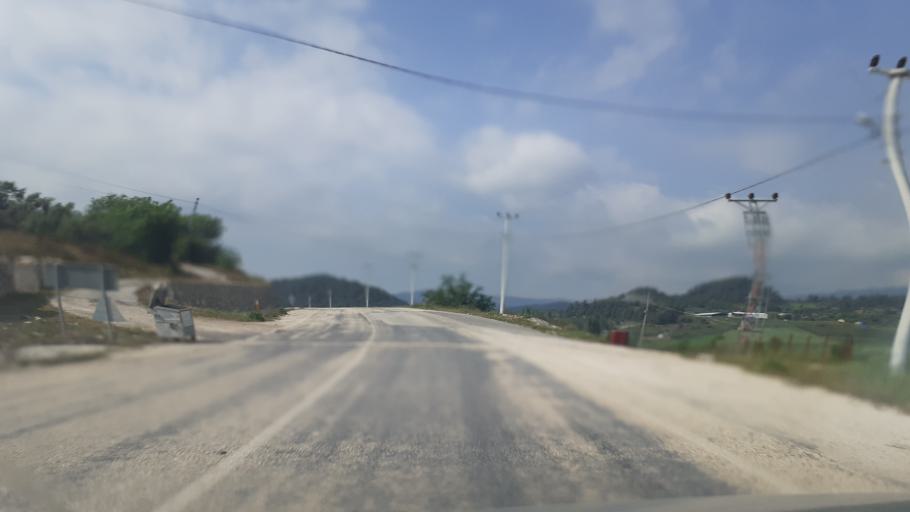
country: TR
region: Hatay
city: Yayladagi
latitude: 35.9105
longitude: 36.0541
